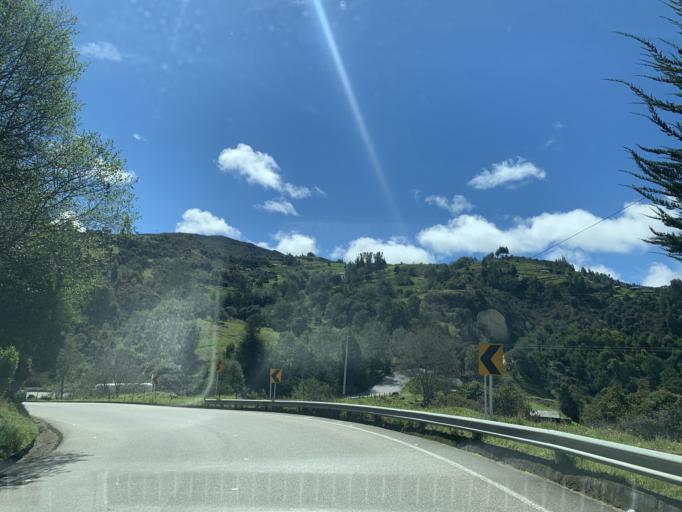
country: CO
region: Boyaca
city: Aquitania
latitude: 5.6159
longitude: -72.8776
